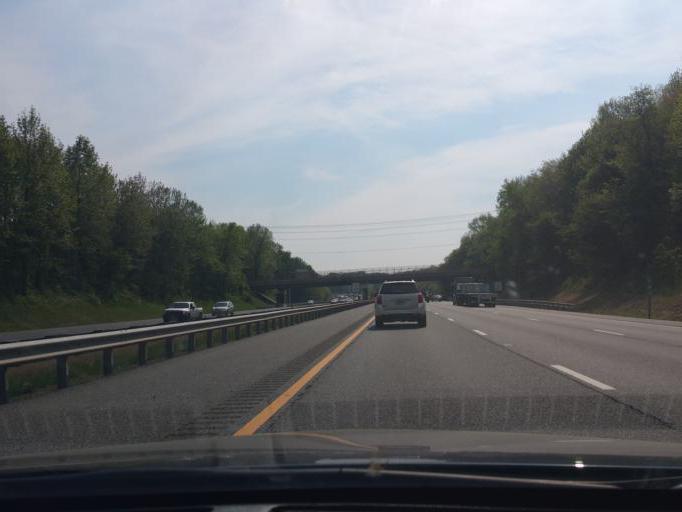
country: US
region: Maryland
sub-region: Harford County
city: Riverside
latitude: 39.4793
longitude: -76.2648
